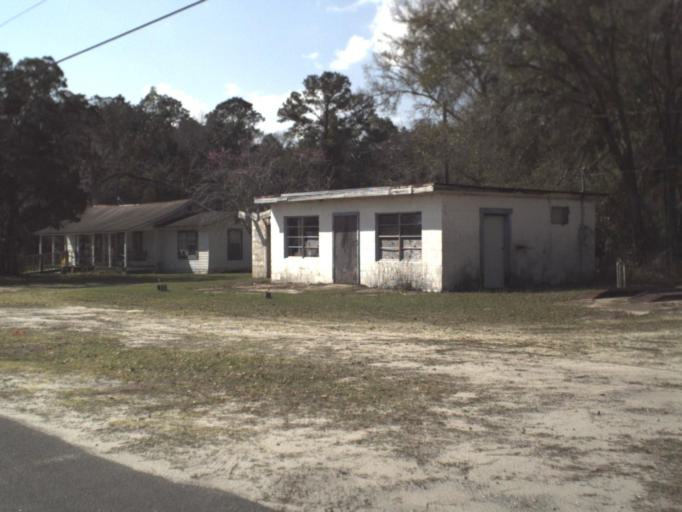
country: US
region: Florida
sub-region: Wakulla County
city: Crawfordville
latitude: 30.0761
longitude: -84.4269
